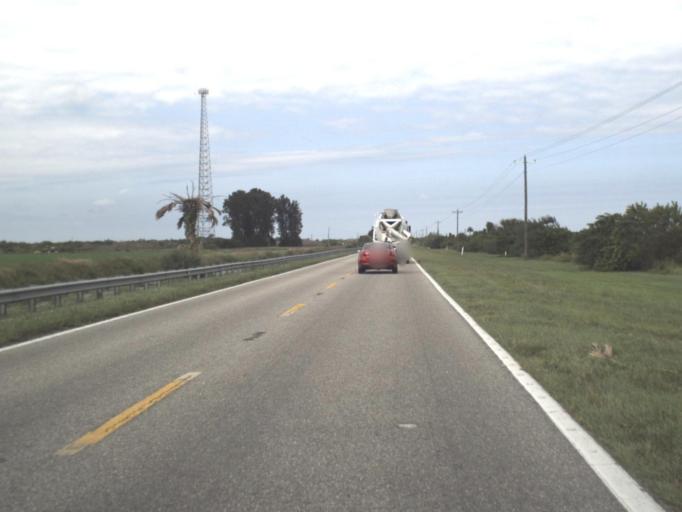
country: US
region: Florida
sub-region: Glades County
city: Moore Haven
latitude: 26.7628
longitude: -81.1638
